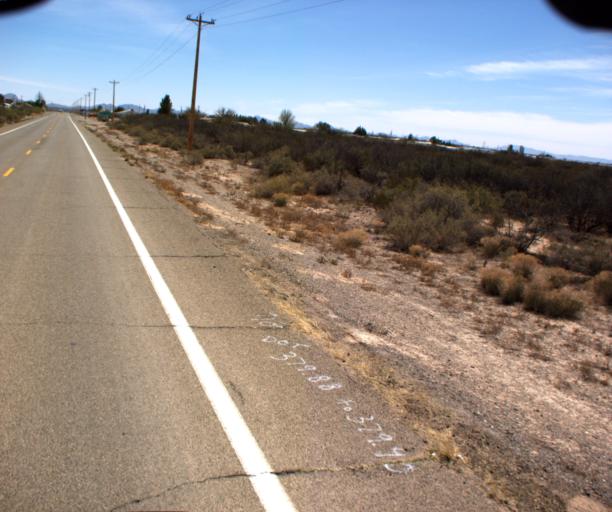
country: US
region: New Mexico
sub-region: Hidalgo County
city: Lordsburg
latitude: 32.2682
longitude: -109.2345
